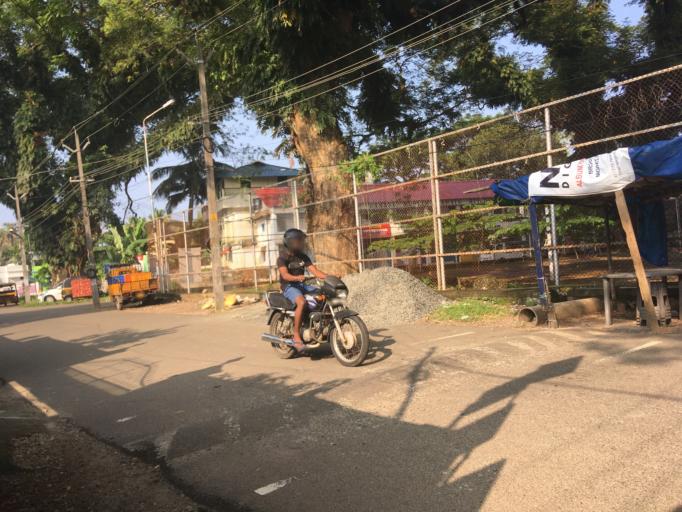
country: IN
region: Kerala
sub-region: Ernakulam
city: Cochin
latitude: 9.9610
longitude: 76.2407
